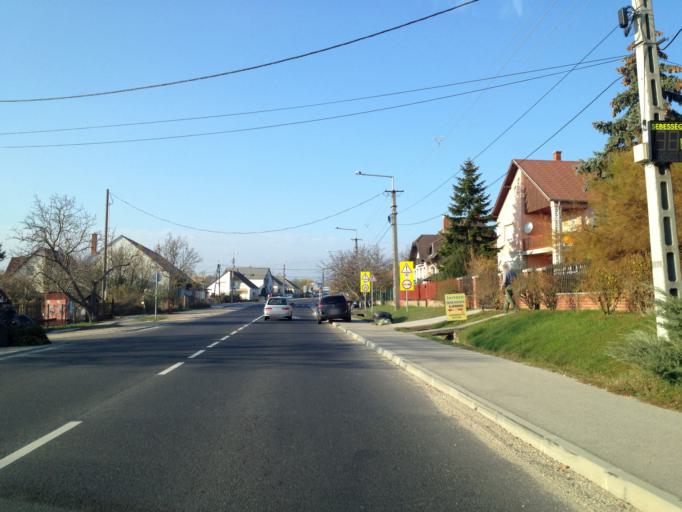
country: HU
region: Veszprem
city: Veszprem
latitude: 47.1430
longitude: 17.9503
